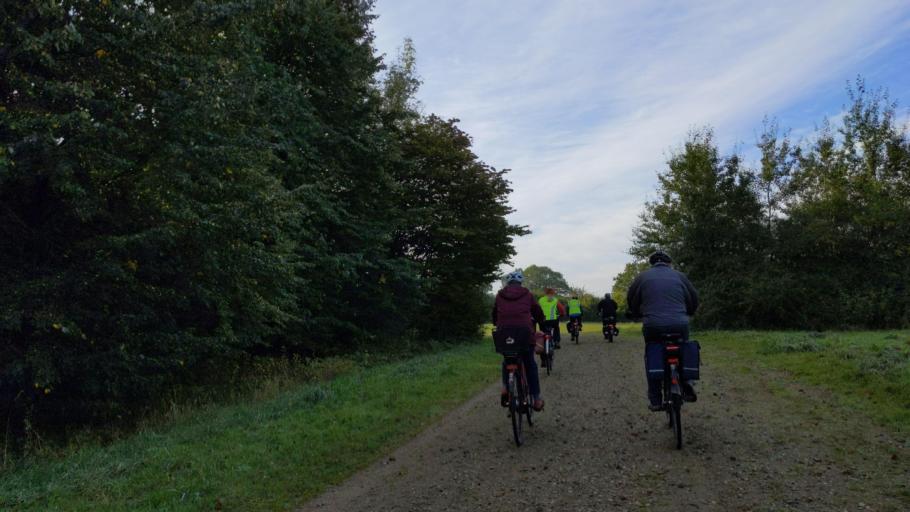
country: DE
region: Schleswig-Holstein
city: Badendorf
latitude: 53.8764
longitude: 10.5863
